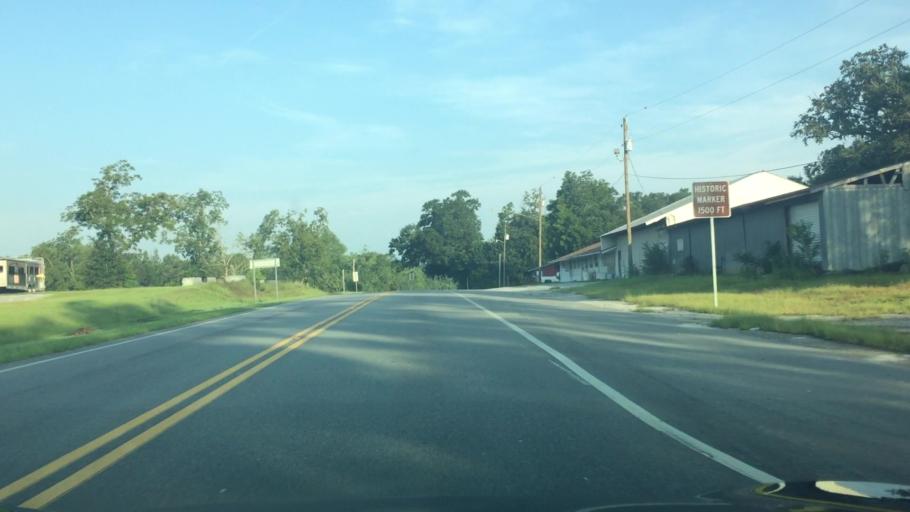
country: US
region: Alabama
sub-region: Covington County
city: Florala
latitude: 31.0112
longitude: -86.3519
